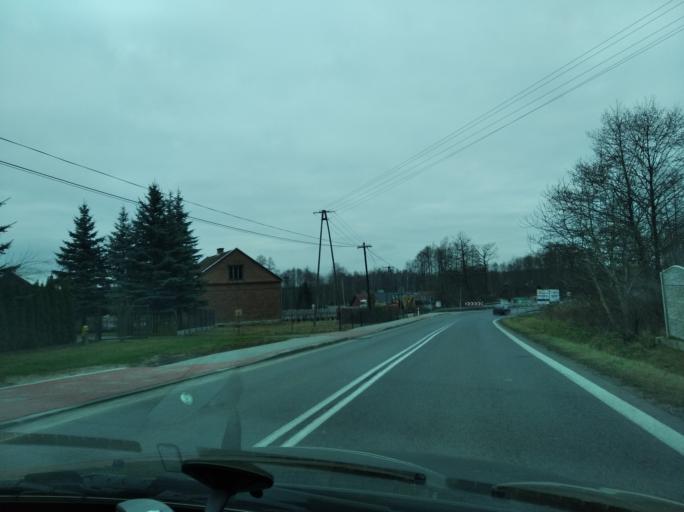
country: PL
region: Subcarpathian Voivodeship
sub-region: Powiat lancucki
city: Zolynia
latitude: 50.1492
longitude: 22.2747
